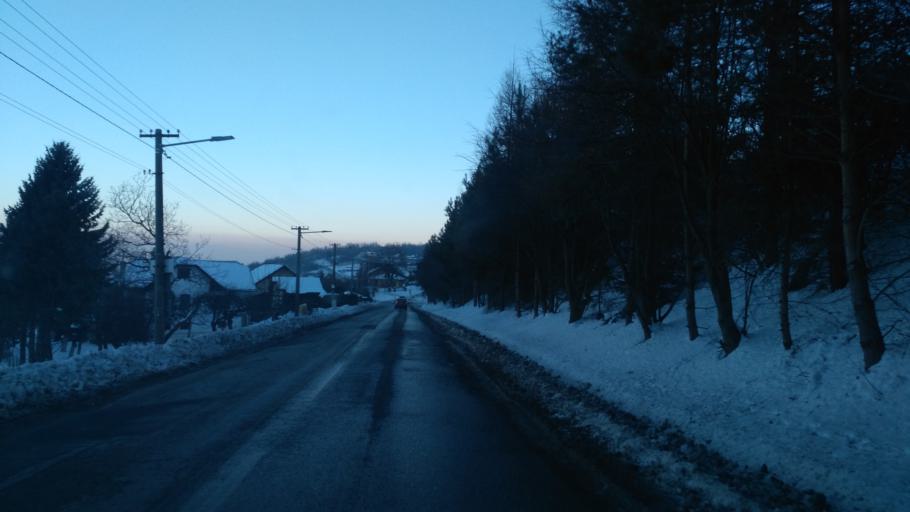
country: SK
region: Kosicky
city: Kosice
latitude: 48.7736
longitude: 21.2083
